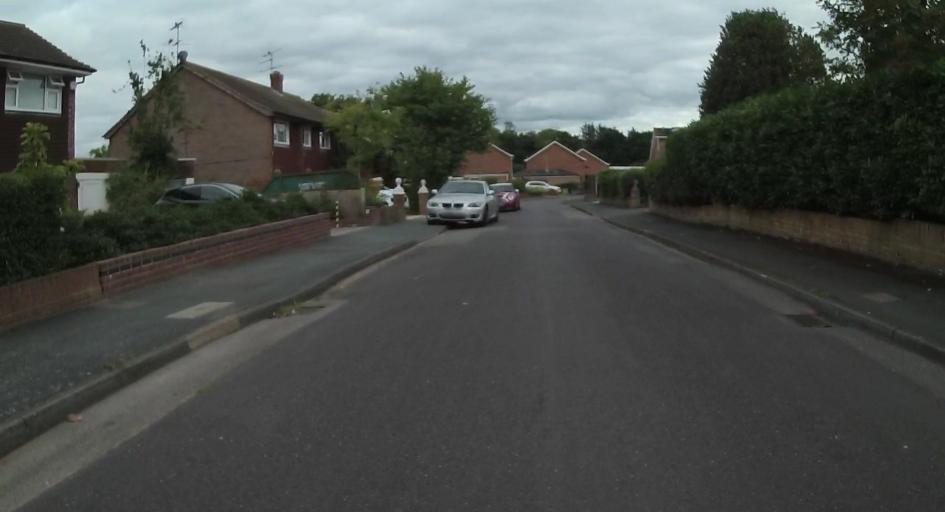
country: GB
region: England
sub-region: Surrey
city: Knaphill
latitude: 51.3253
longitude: -0.6332
